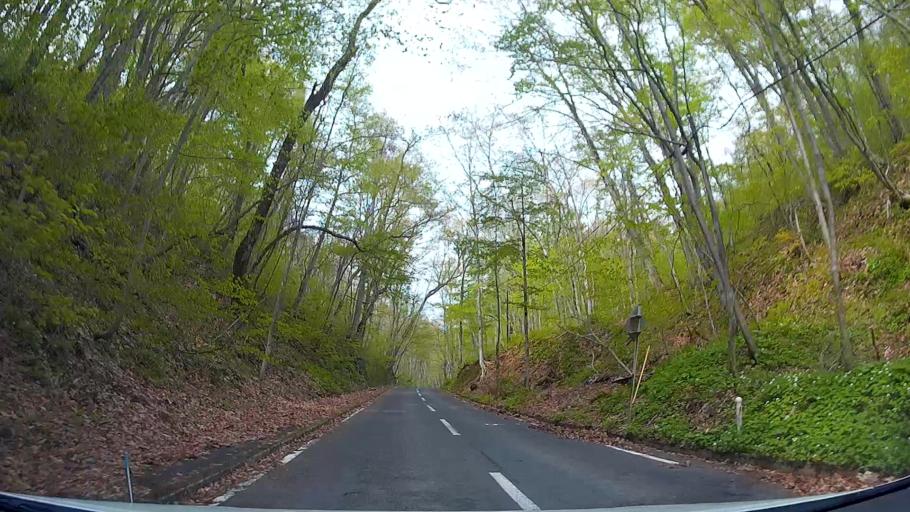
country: JP
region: Akita
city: Hanawa
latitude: 40.4257
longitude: 140.9116
